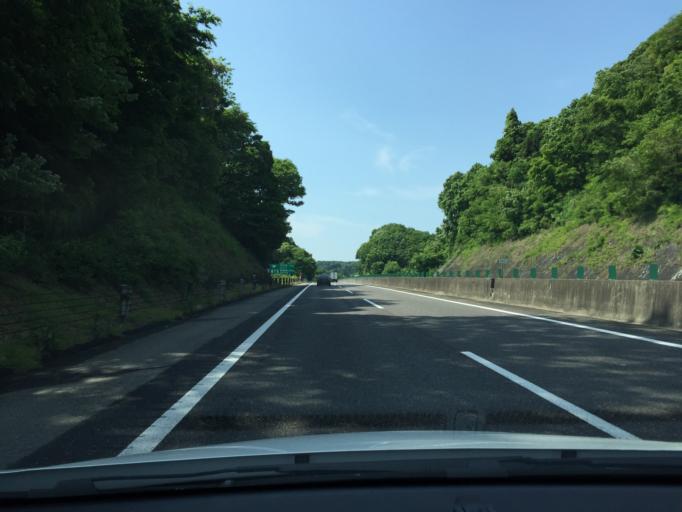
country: JP
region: Fukushima
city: Sukagawa
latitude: 37.1696
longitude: 140.2706
